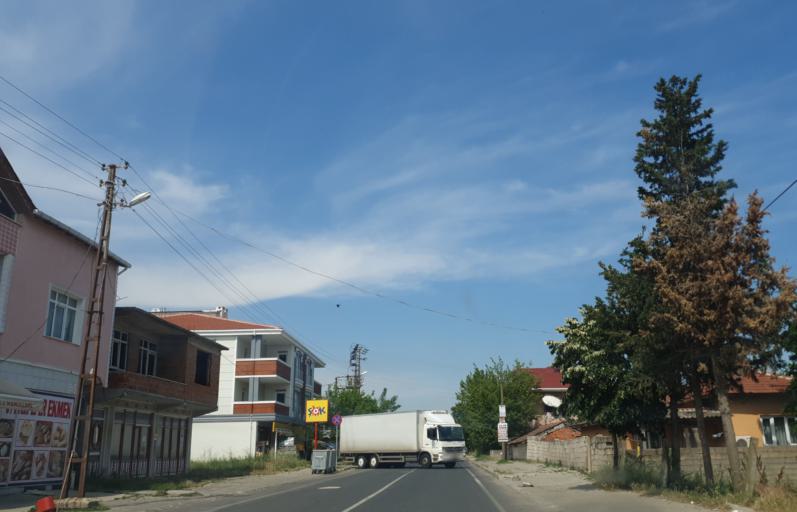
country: TR
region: Tekirdag
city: Beyazkoy
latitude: 41.2632
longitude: 27.6490
